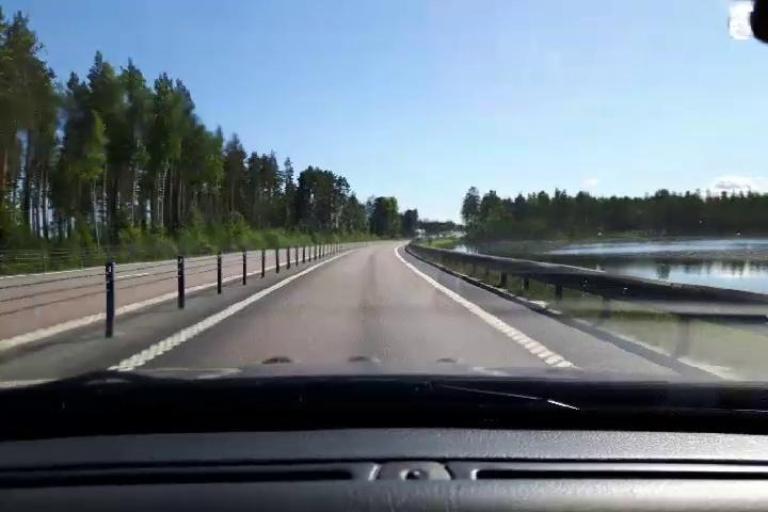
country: SE
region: Gaevleborg
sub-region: Gavle Kommun
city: Norrsundet
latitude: 61.0806
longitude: 16.9715
